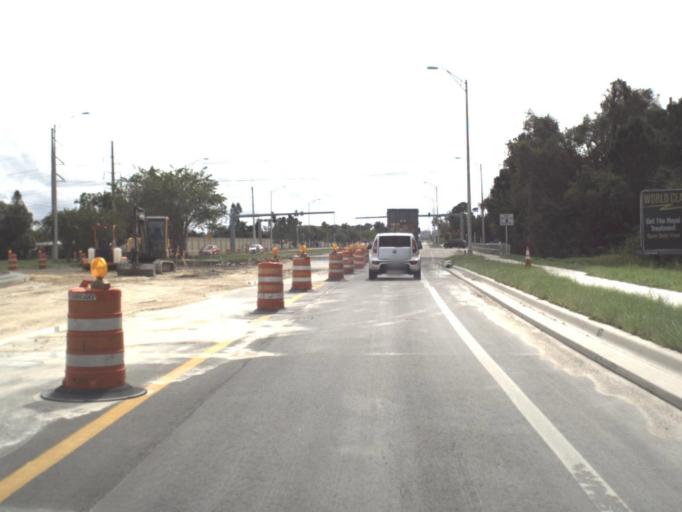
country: US
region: Florida
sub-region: Lee County
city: Palmona Park
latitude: 26.6984
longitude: -81.8909
